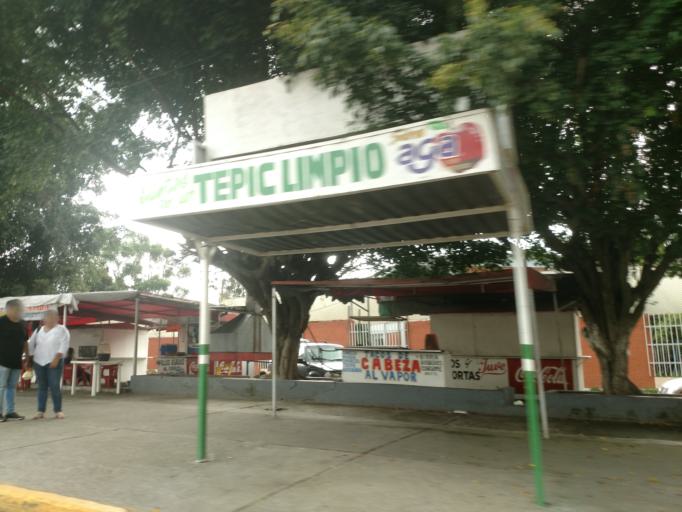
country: MX
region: Nayarit
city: Tepic
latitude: 21.4834
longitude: -104.8818
